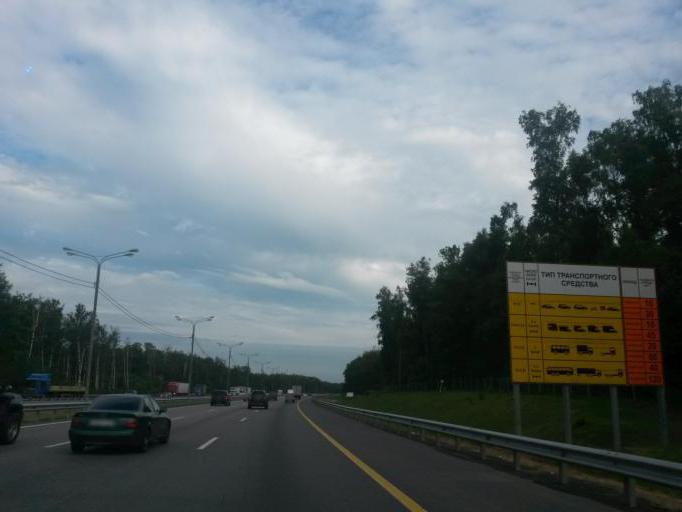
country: RU
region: Moskovskaya
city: Vostryakovo
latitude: 55.3588
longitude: 37.7972
